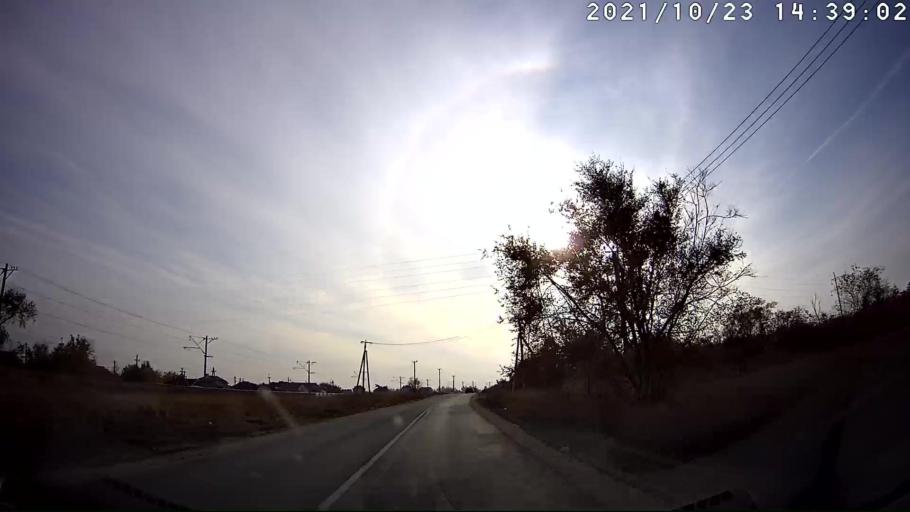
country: RU
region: Volgograd
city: Krasnoslobodsk
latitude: 48.4879
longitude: 44.5480
